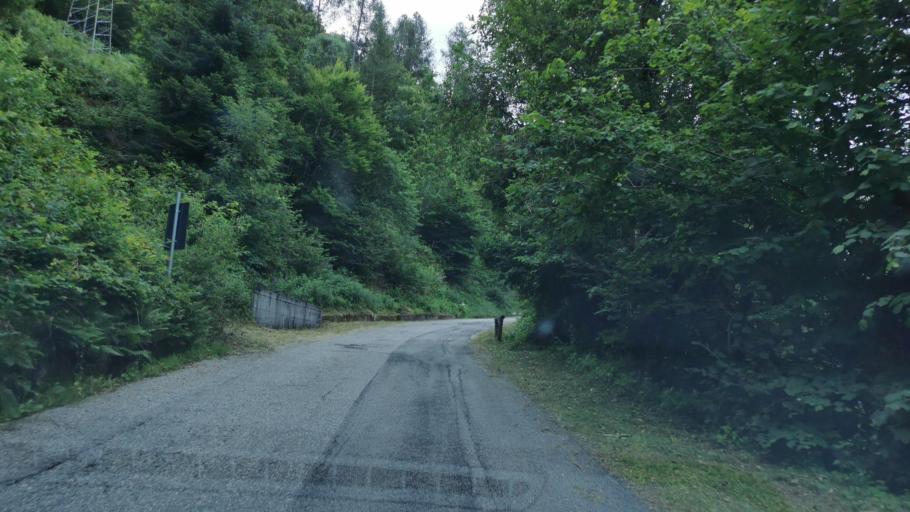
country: IT
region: Lombardy
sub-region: Provincia di Lecco
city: Casargo
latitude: 46.0424
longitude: 9.3956
